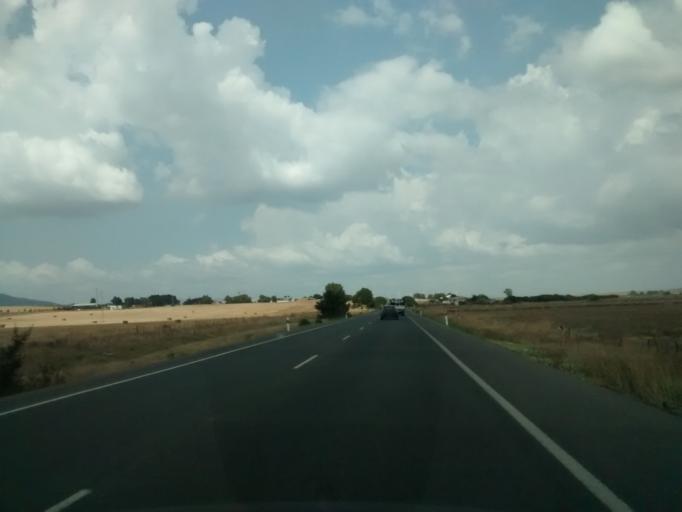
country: ES
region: Andalusia
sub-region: Provincia de Cadiz
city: Zahara de los Atunes
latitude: 36.1773
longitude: -5.7479
